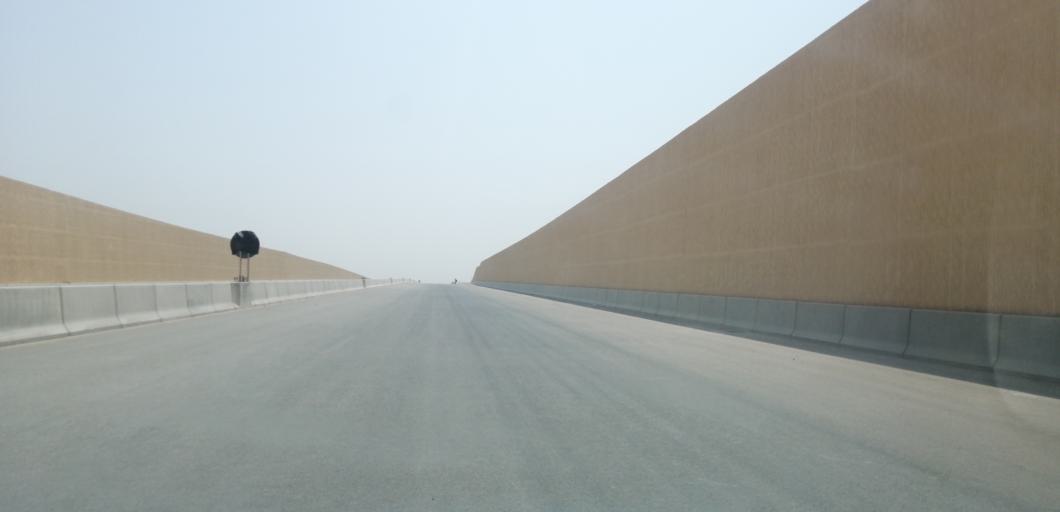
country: KW
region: Muhafazat al Jahra'
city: Al Jahra'
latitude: 29.4536
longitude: 47.5601
